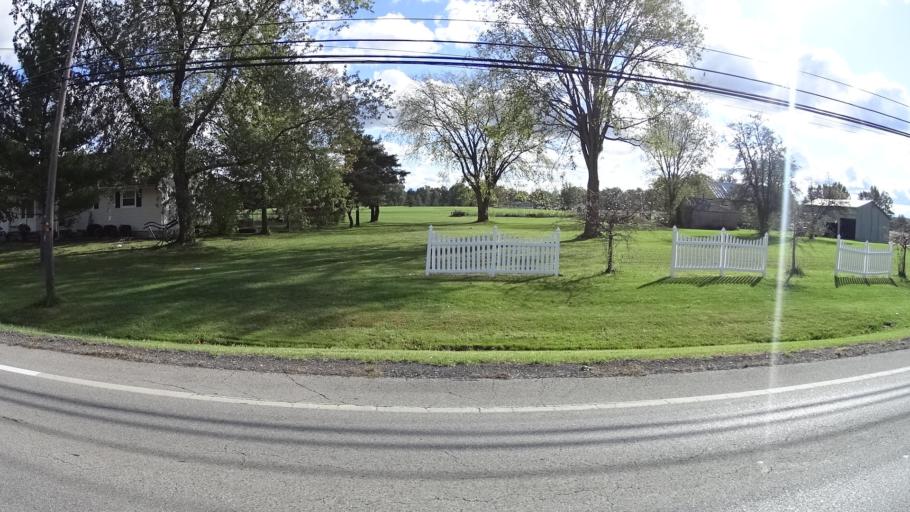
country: US
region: Ohio
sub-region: Lorain County
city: Grafton
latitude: 41.3077
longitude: -82.0700
